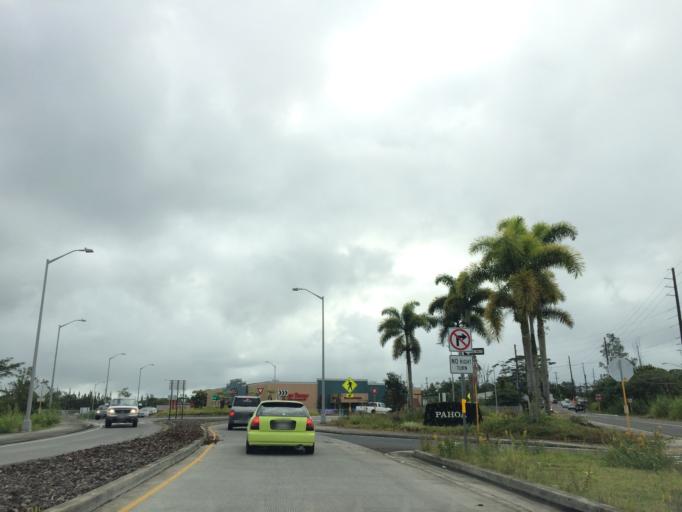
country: US
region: Hawaii
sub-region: Hawaii County
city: Hawaiian Paradise Park
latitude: 19.5057
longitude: -154.9568
